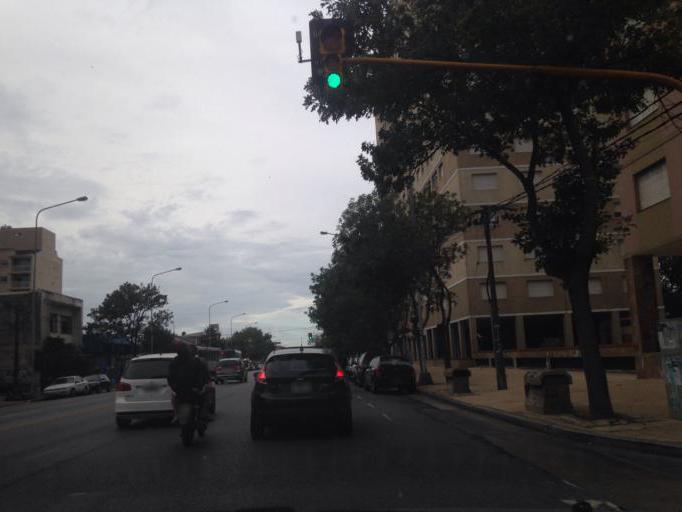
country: AR
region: Buenos Aires
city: Mar del Plata
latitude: -38.0180
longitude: -57.5704
